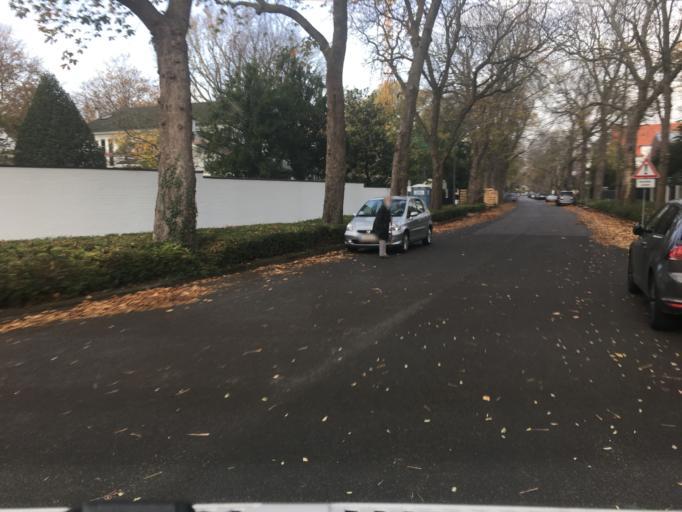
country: DE
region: North Rhine-Westphalia
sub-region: Regierungsbezirk Koln
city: Bayenthal
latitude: 50.8982
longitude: 6.9720
